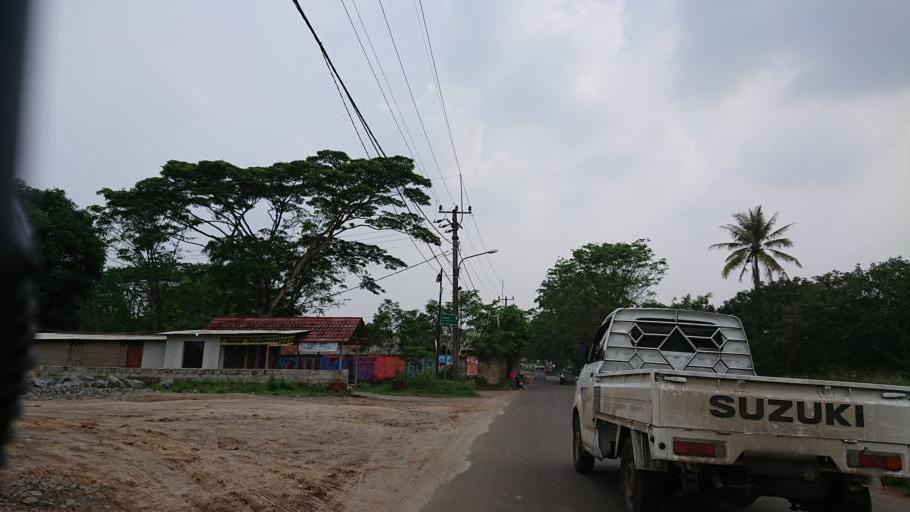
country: ID
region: West Java
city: Parung
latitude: -6.4569
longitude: 106.7056
